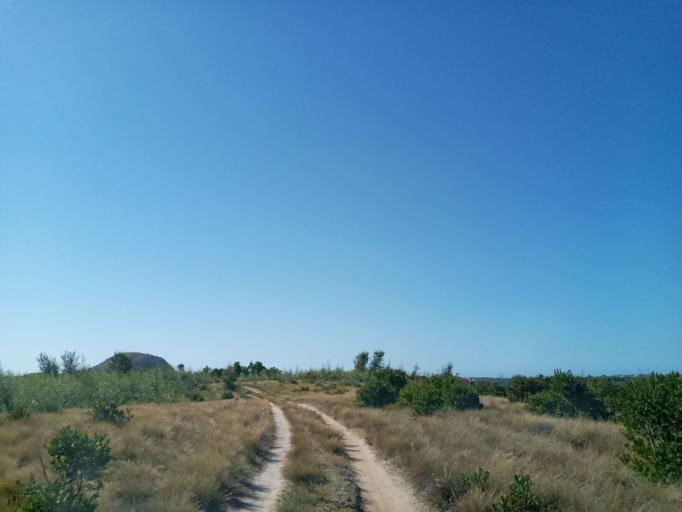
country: MG
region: Anosy
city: Fort Dauphin
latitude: -24.9126
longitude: 47.0886
